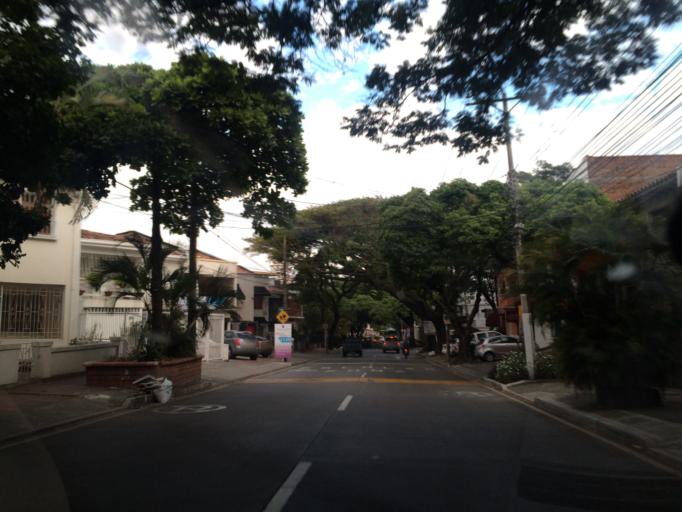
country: CO
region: Valle del Cauca
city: Cali
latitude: 3.4354
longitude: -76.5434
